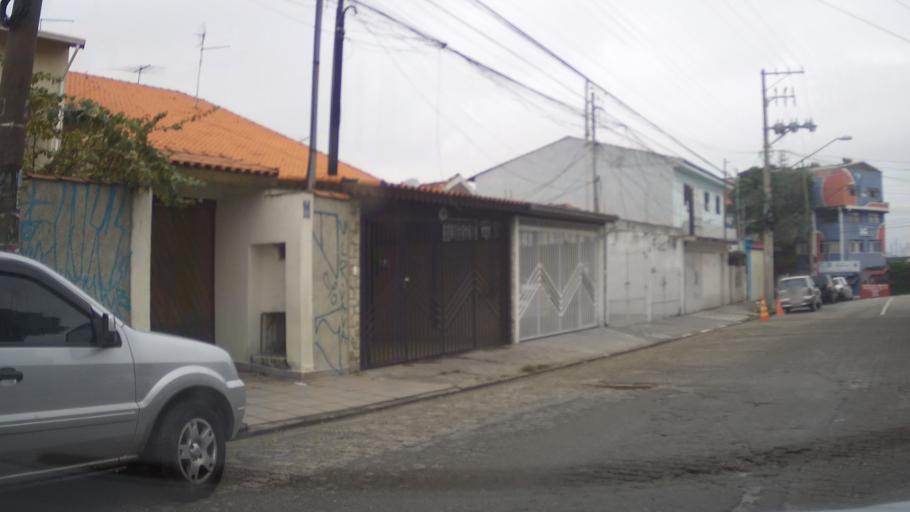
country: BR
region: Sao Paulo
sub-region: Guarulhos
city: Guarulhos
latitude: -23.4945
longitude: -46.5514
